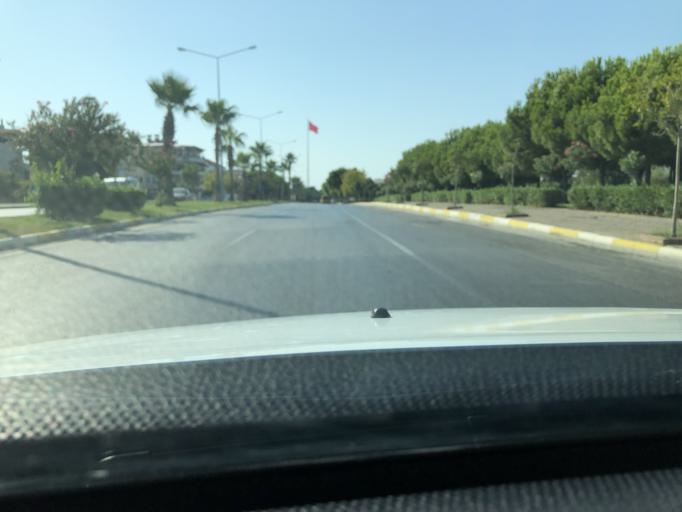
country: TR
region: Antalya
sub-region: Manavgat
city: Side
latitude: 36.7797
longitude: 31.3946
